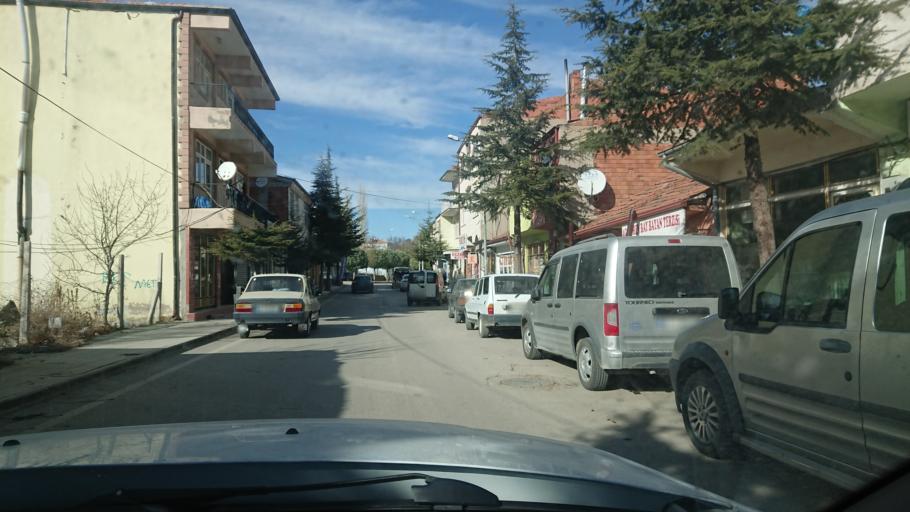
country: TR
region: Aksaray
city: Agacoren
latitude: 38.8703
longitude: 33.9146
